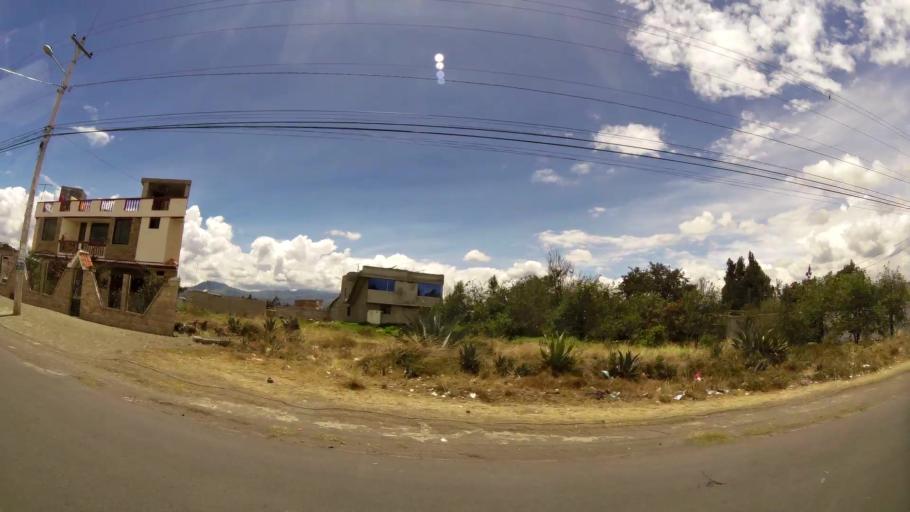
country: EC
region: Tungurahua
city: Ambato
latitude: -1.2731
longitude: -78.5908
